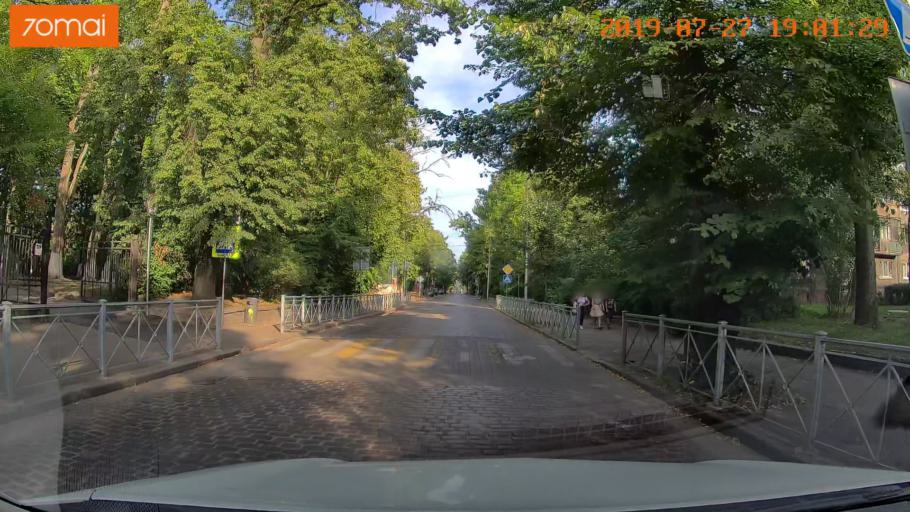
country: RU
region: Kaliningrad
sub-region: Gorod Kaliningrad
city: Kaliningrad
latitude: 54.7263
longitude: 20.4888
